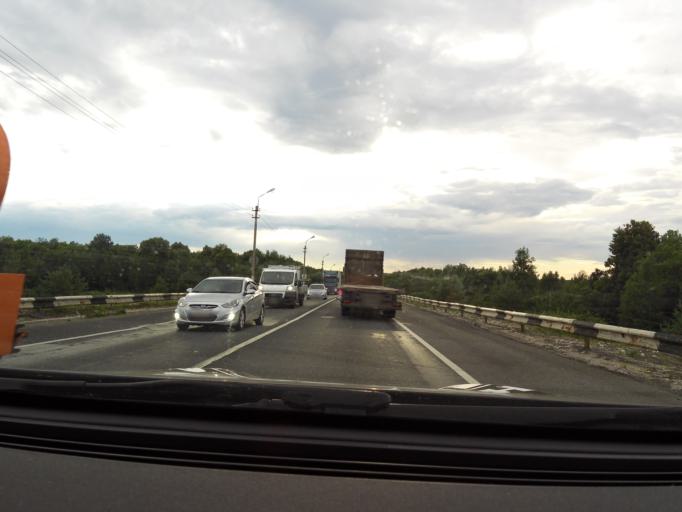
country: RU
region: Vladimir
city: Kommunar
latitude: 56.0562
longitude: 40.3989
